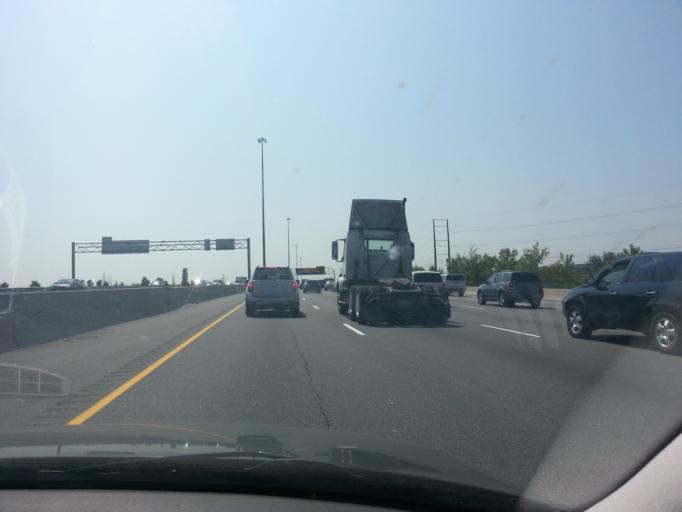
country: CA
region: Ontario
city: Burlington
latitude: 43.3477
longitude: -79.8097
